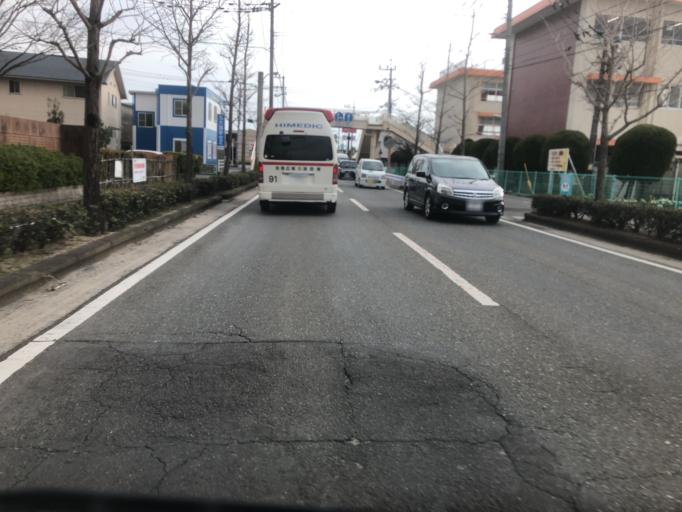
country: JP
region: Saga Prefecture
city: Saga-shi
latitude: 33.2749
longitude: 130.2707
